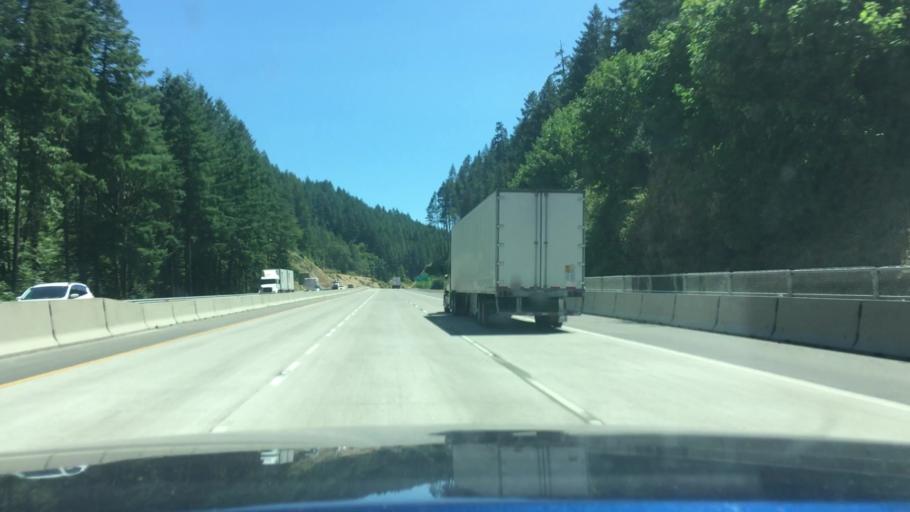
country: US
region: Oregon
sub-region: Douglas County
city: Drain
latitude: 43.6969
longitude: -123.2020
